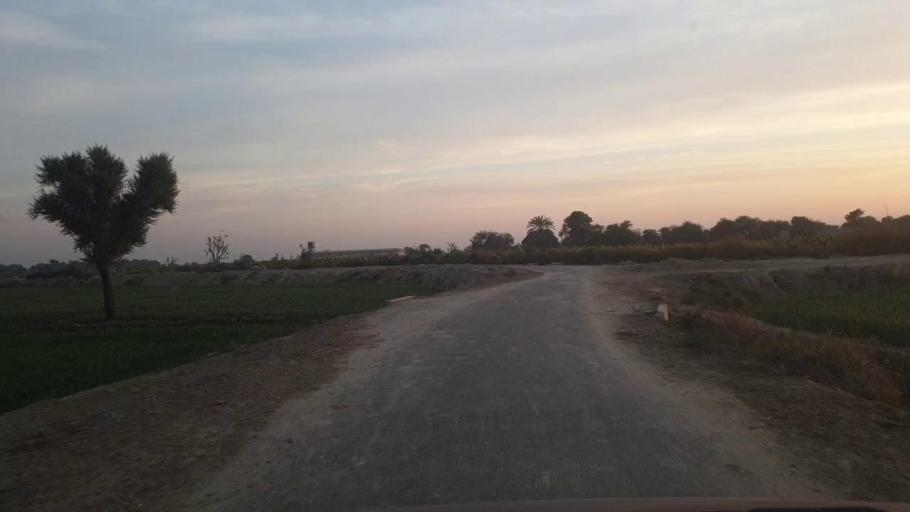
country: PK
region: Sindh
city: Shahpur Chakar
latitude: 26.0736
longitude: 68.5248
